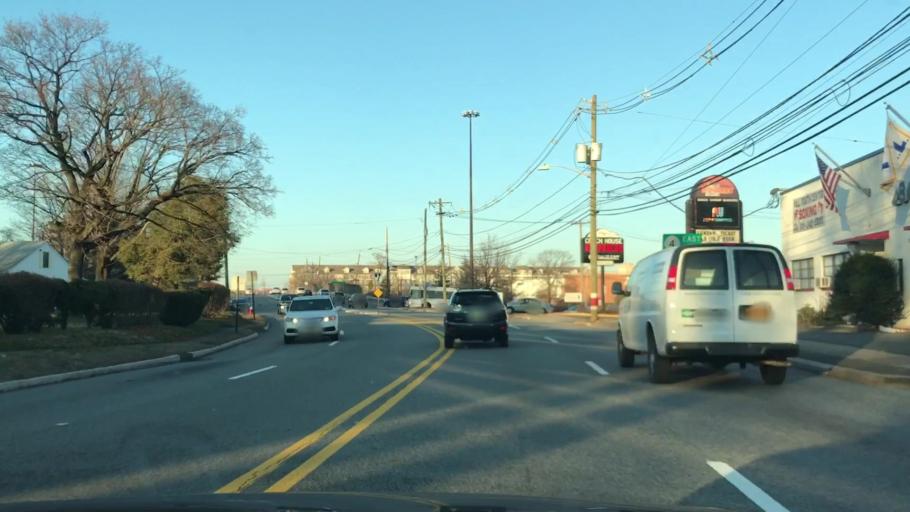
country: US
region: New Jersey
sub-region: Bergen County
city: Teaneck
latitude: 40.9041
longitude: -74.0336
